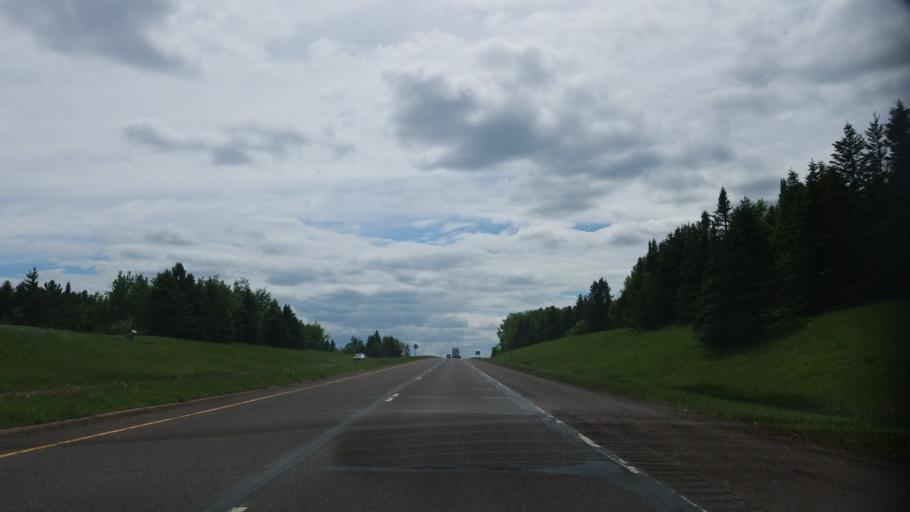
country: US
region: Minnesota
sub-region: Lake County
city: Two Harbors
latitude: 47.0166
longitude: -91.7033
